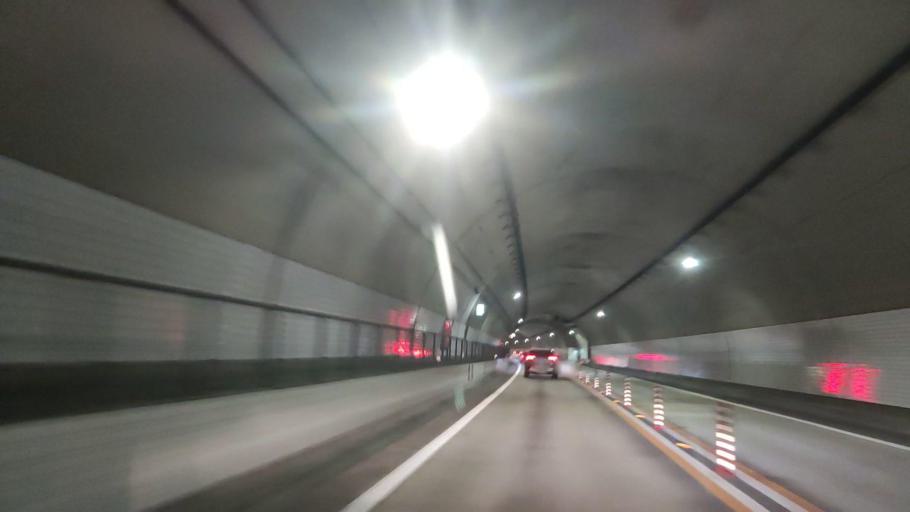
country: JP
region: Kyoto
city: Miyazu
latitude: 35.5622
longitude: 135.1218
